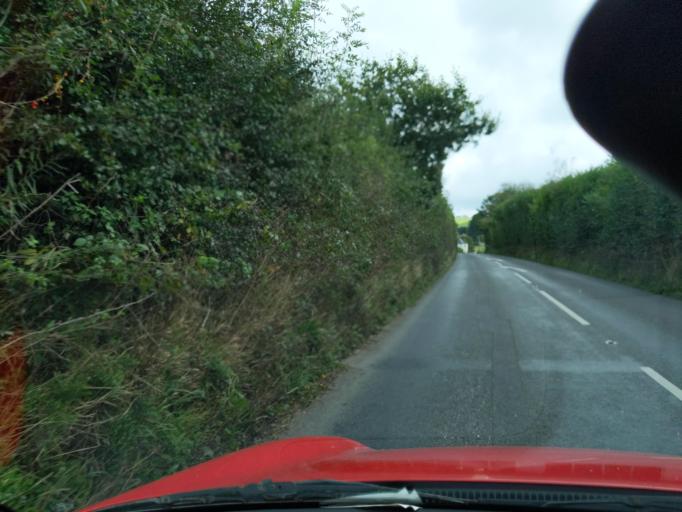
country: GB
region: England
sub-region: Devon
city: Modbury
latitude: 50.3442
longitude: -3.8818
